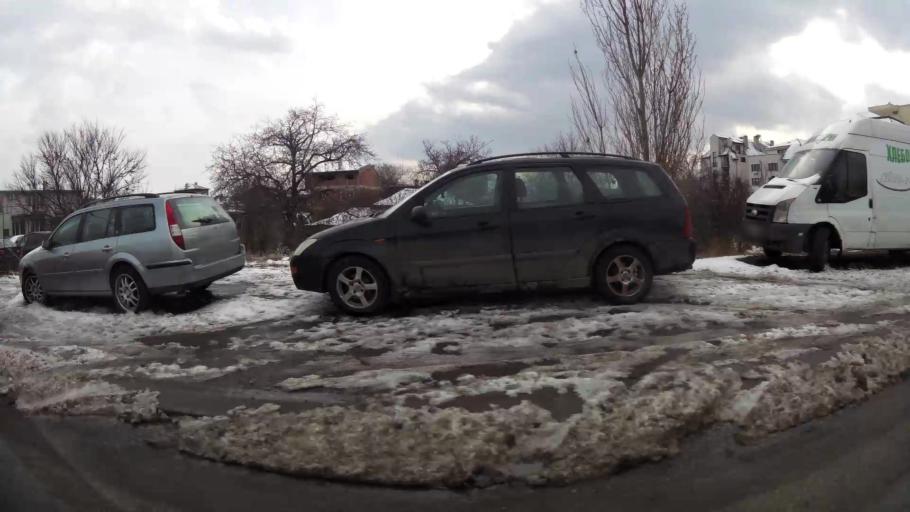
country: BG
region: Sofia-Capital
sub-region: Stolichna Obshtina
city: Sofia
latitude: 42.7085
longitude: 23.3718
